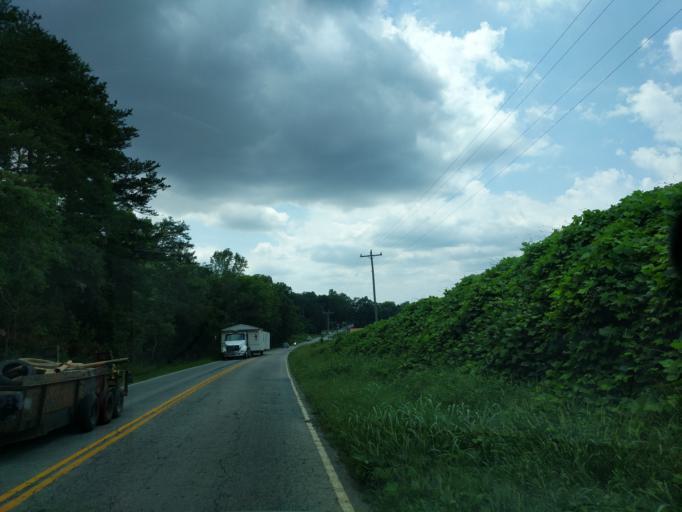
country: US
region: South Carolina
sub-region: Spartanburg County
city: Wellford
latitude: 34.9838
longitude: -82.1125
